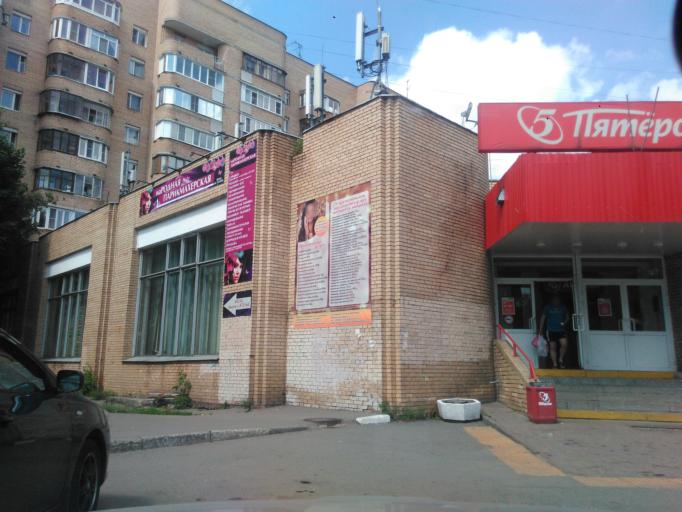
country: RU
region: Moscow
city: Vagonoremont
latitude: 55.8939
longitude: 37.5350
